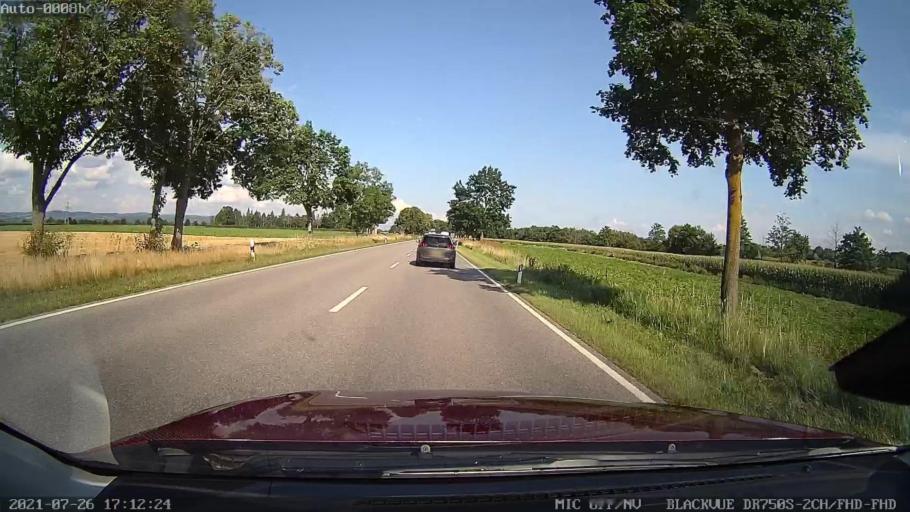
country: DE
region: Bavaria
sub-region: Upper Palatinate
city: Mintraching
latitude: 48.9744
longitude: 12.3030
